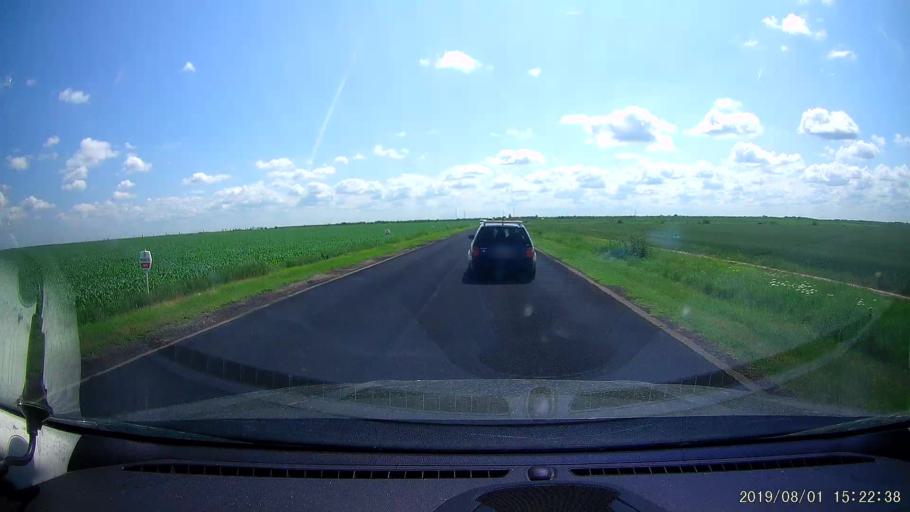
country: RO
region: Braila
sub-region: Comuna Viziru
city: Lanurile
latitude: 45.0511
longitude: 27.7731
